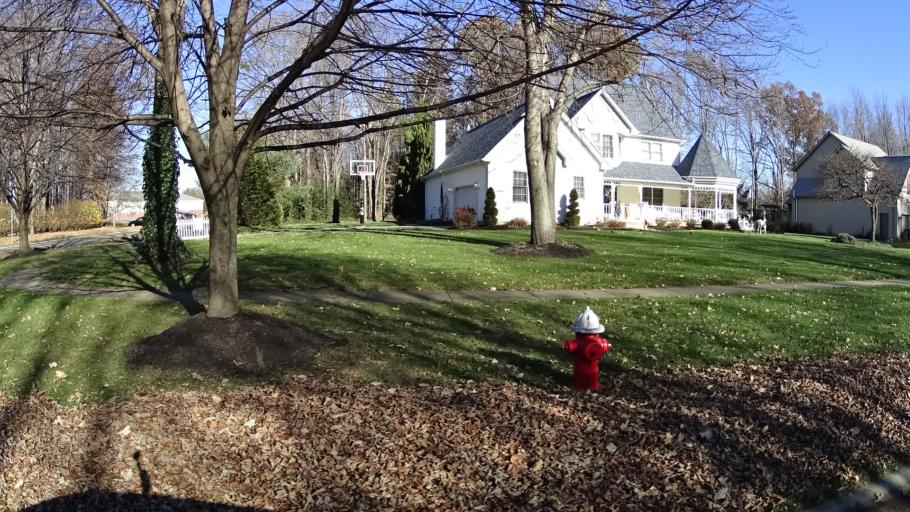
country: US
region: Ohio
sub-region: Lorain County
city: Avon
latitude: 41.4425
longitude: -82.0355
